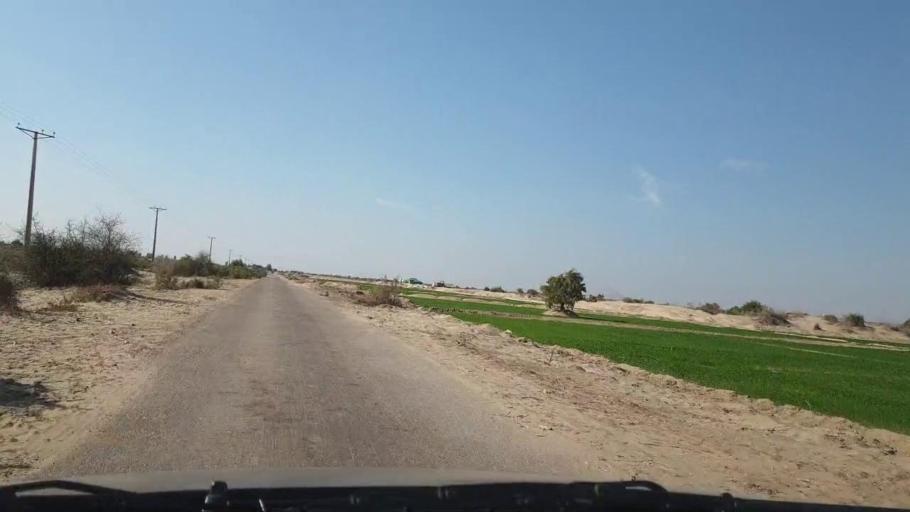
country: PK
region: Sindh
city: Khadro
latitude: 26.2687
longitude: 68.7943
